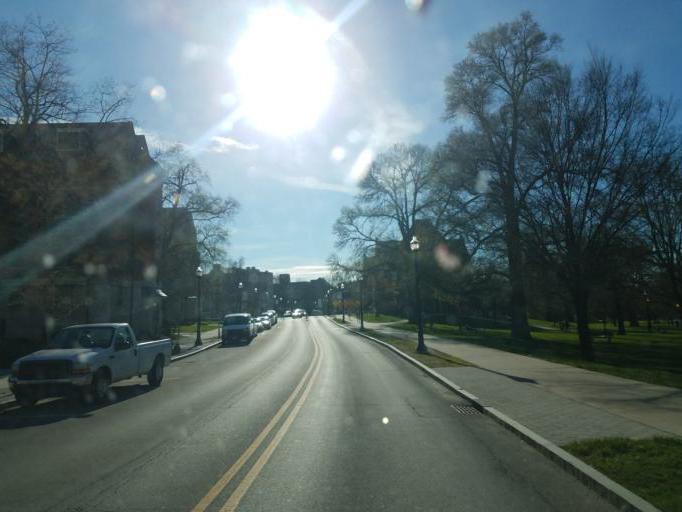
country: US
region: Ohio
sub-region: Franklin County
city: Grandview Heights
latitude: 39.9970
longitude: -83.0100
